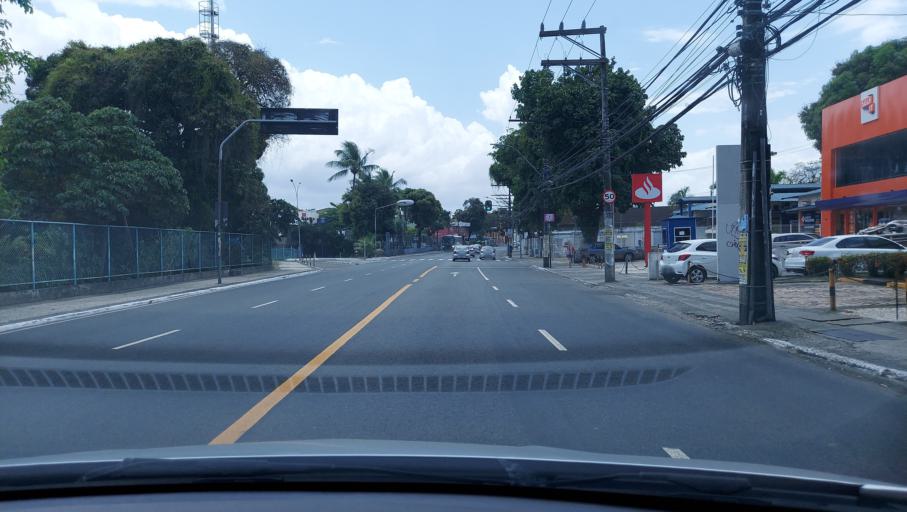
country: BR
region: Bahia
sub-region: Salvador
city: Salvador
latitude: -12.9635
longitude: -38.4720
